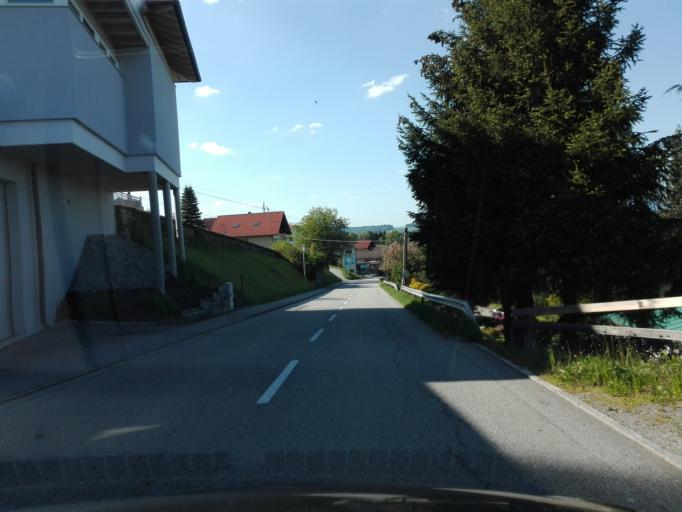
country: DE
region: Bavaria
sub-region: Lower Bavaria
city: Obernzell
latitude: 48.5306
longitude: 13.6479
